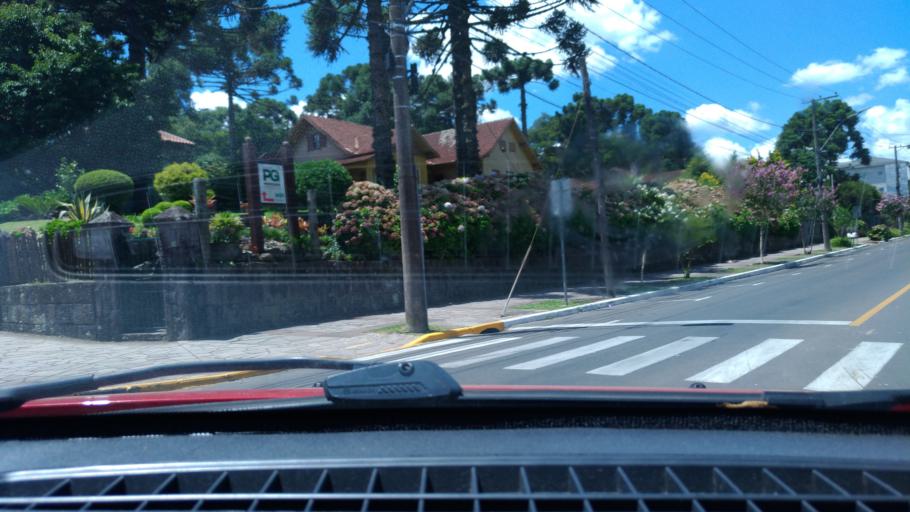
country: BR
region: Rio Grande do Sul
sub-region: Canela
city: Canela
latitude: -29.3618
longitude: -50.8114
